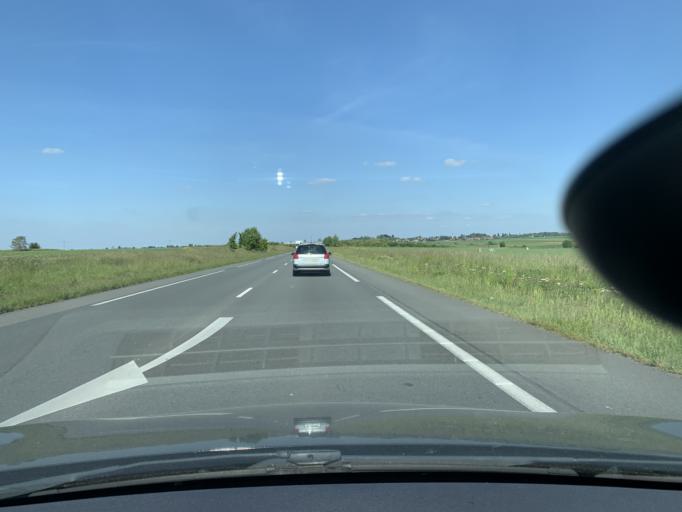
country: FR
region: Nord-Pas-de-Calais
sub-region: Departement du Nord
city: Rumilly-en-Cambresis
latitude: 50.1424
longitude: 3.2239
